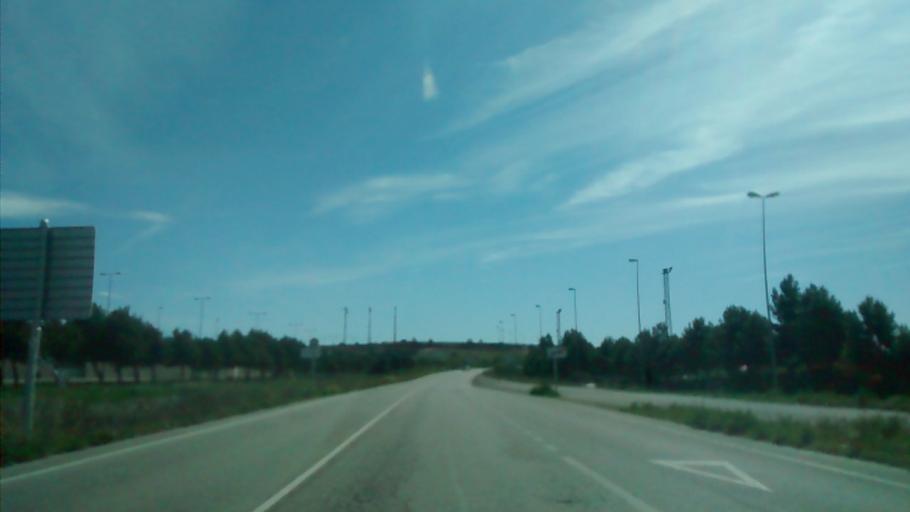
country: ES
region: Catalonia
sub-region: Provincia de Lleida
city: Maials
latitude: 41.3649
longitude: 0.5095
